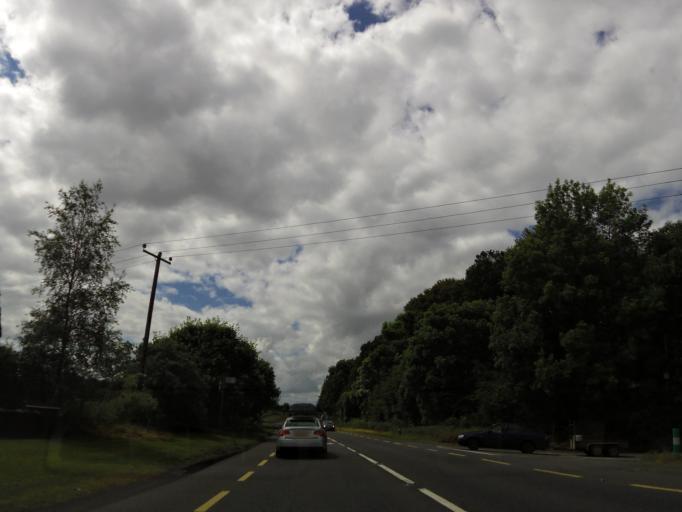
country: IE
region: Munster
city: Nenagh Bridge
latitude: 52.9240
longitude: -8.1706
